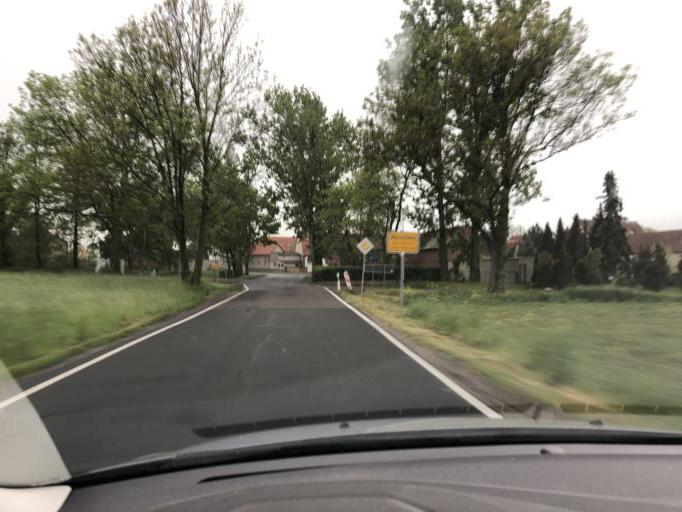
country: DE
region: Saxony
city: Krostitz
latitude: 51.4401
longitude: 12.4927
